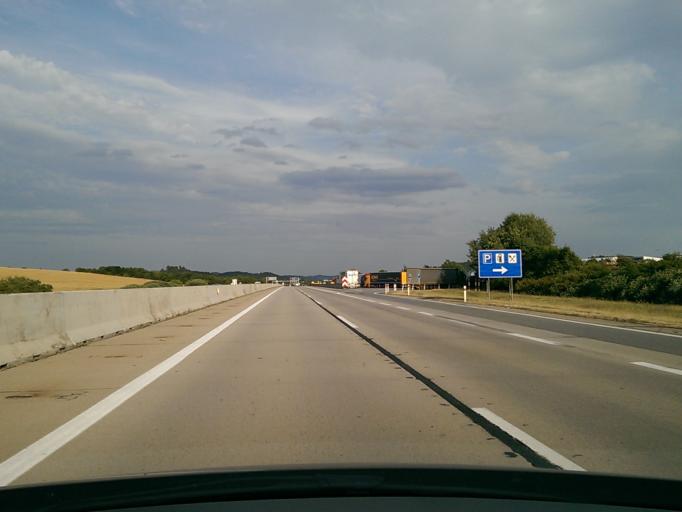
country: CZ
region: Vysocina
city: Merin
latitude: 49.3793
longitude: 15.9440
